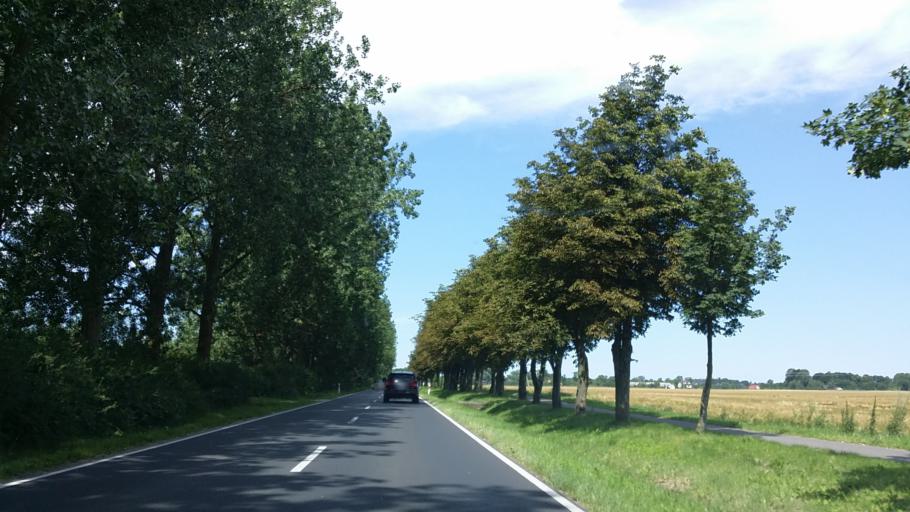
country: PL
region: West Pomeranian Voivodeship
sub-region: Powiat koszalinski
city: Mielno
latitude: 54.2318
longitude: 16.0739
